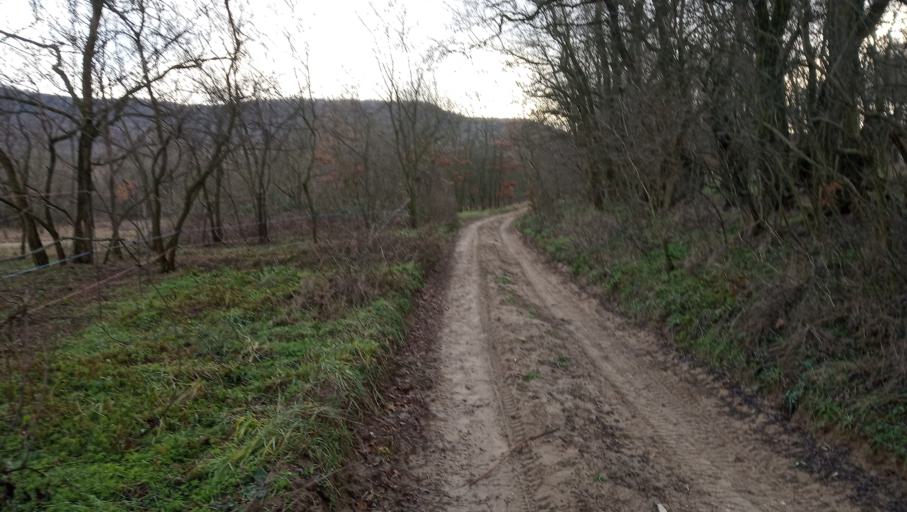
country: HU
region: Komarom-Esztergom
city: Piliscsev
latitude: 47.6695
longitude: 18.8248
